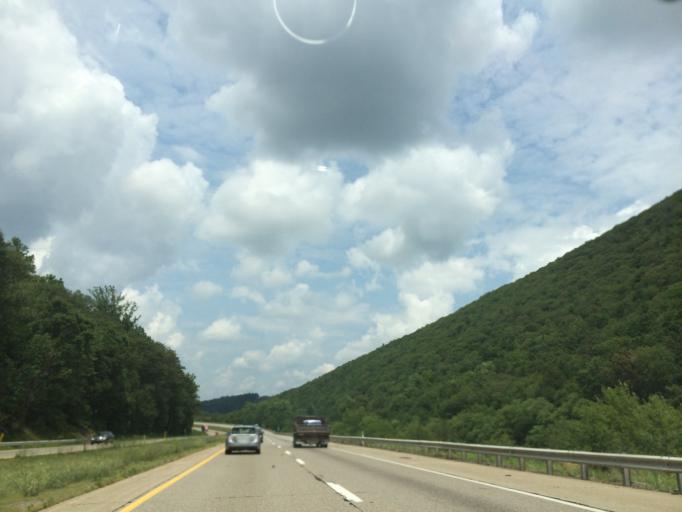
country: US
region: Pennsylvania
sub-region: Luzerne County
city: Nescopeck
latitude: 41.0120
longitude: -76.1671
